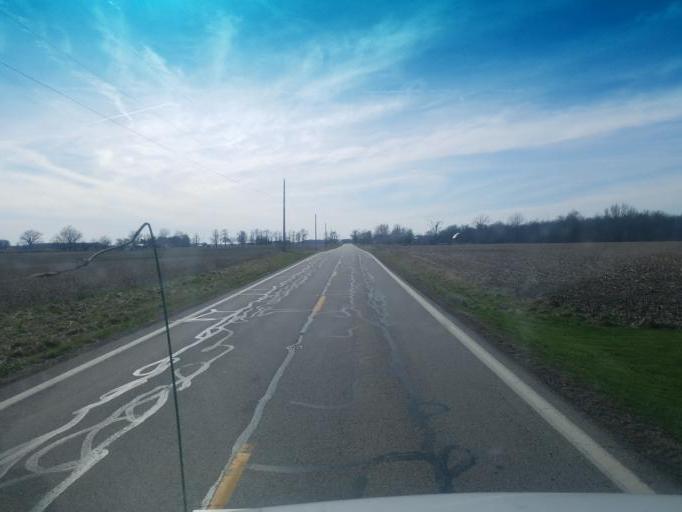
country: US
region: Ohio
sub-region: Union County
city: Richwood
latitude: 40.3490
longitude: -83.3360
